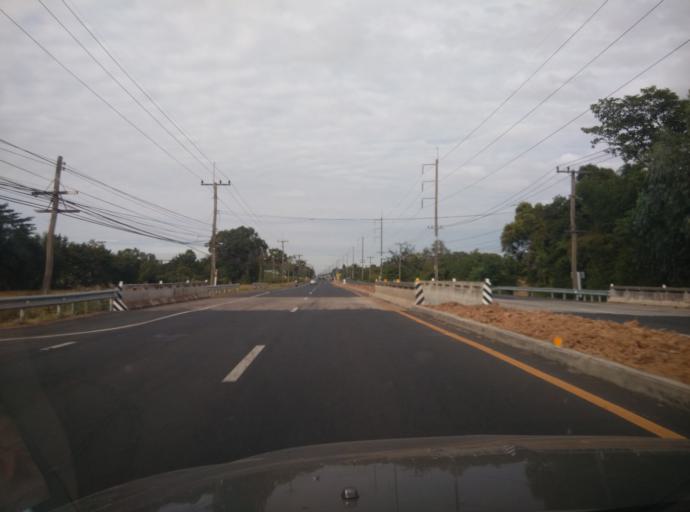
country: TH
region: Sisaket
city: Uthumphon Phisai
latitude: 15.1363
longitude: 104.1489
